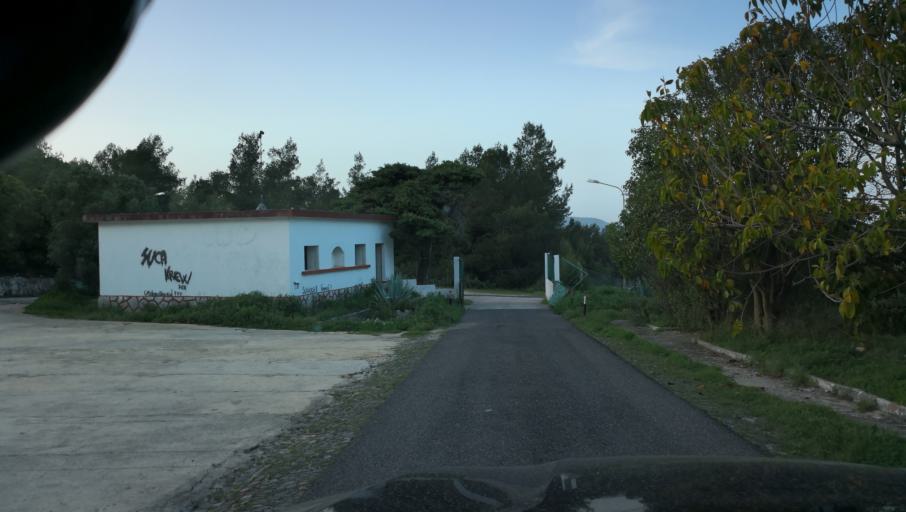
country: PT
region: Setubal
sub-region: Setubal
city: Setubal
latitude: 38.4906
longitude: -8.9374
